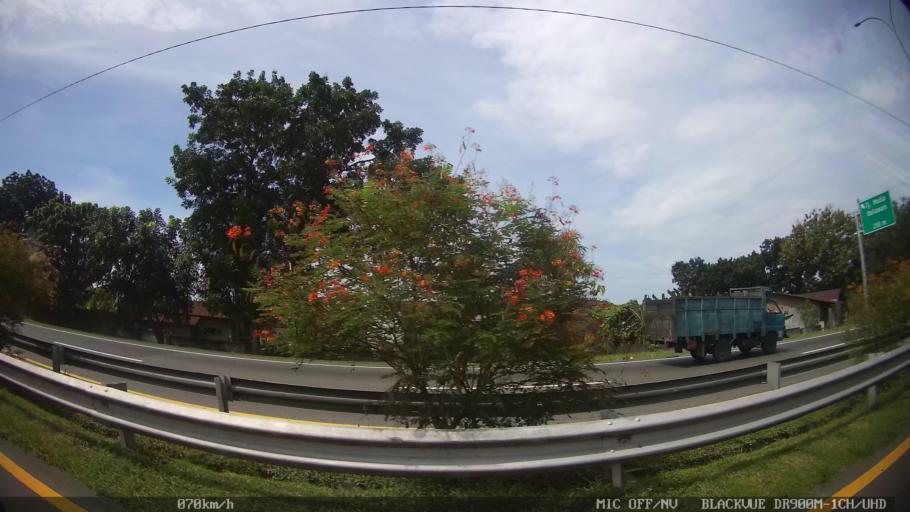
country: ID
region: North Sumatra
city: Medan
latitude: 3.6468
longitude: 98.6860
